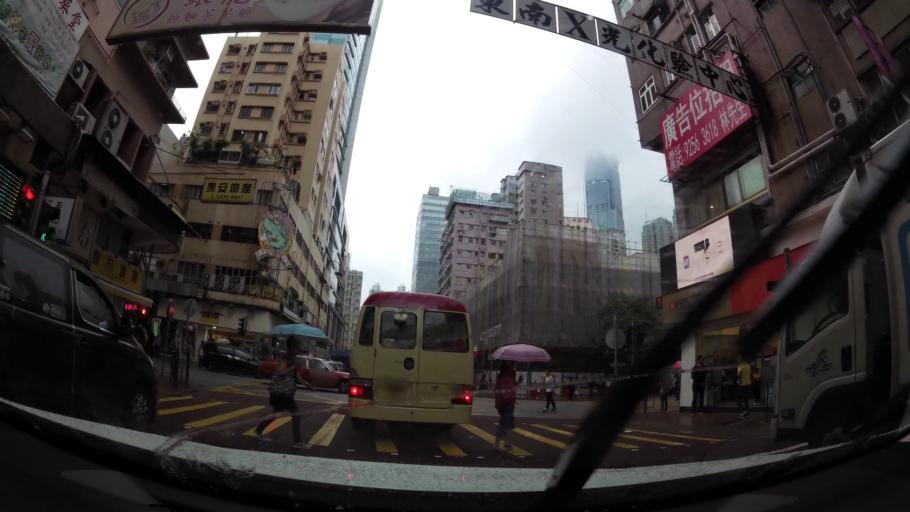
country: HK
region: Tsuen Wan
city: Tsuen Wan
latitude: 22.3716
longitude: 114.1179
